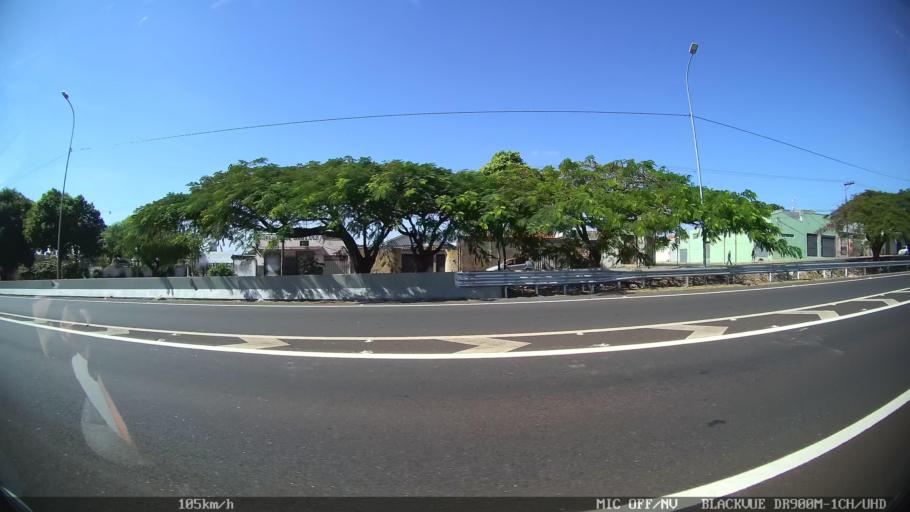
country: BR
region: Sao Paulo
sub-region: Franca
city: Franca
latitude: -20.5005
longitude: -47.4074
